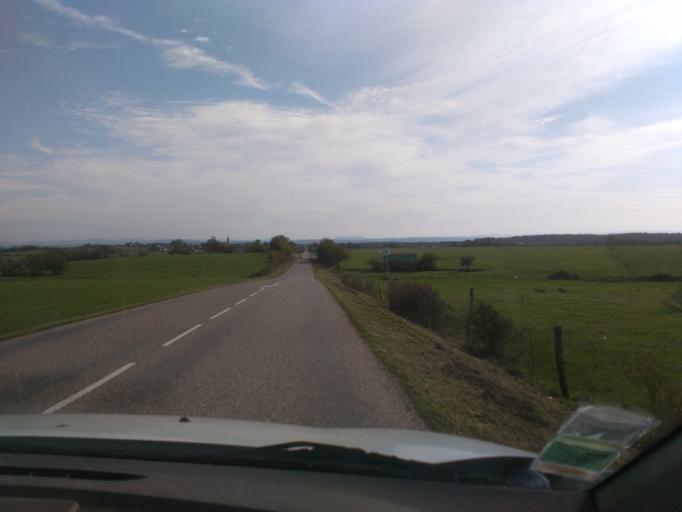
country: FR
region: Lorraine
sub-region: Departement des Vosges
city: Rambervillers
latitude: 48.3509
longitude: 6.5160
